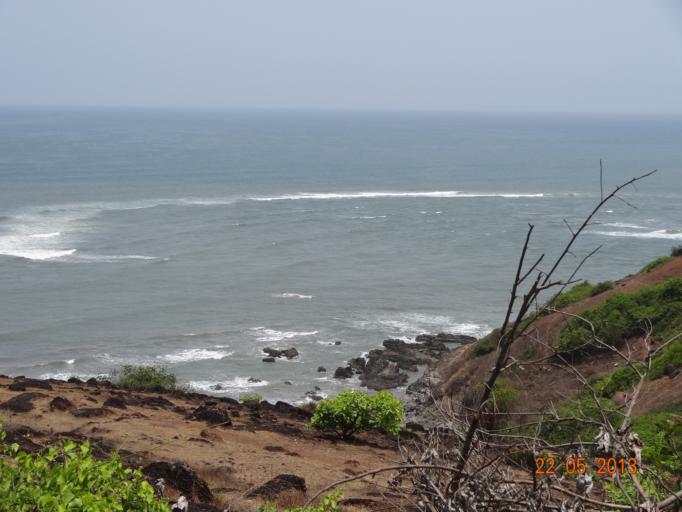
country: IN
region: Goa
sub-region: North Goa
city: Vagator
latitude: 15.6057
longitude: 73.7348
